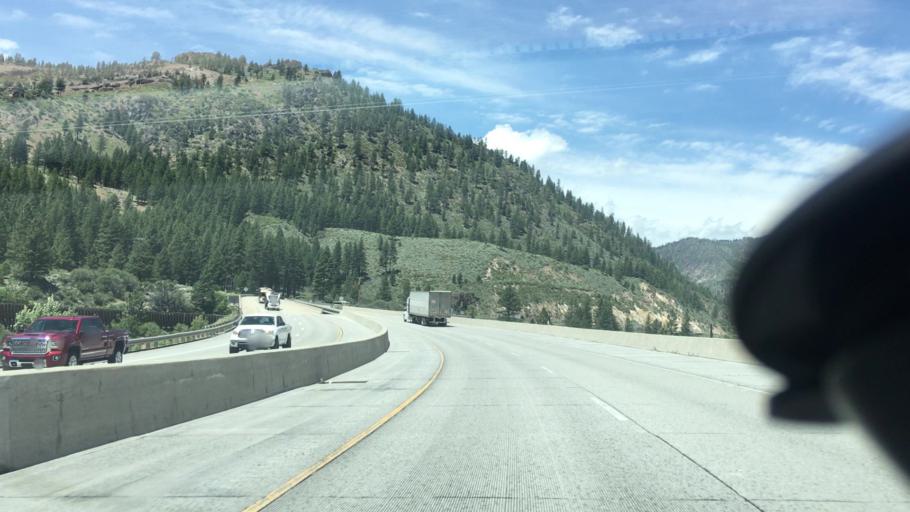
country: US
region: Nevada
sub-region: Washoe County
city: Verdi
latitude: 39.4025
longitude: -120.0230
